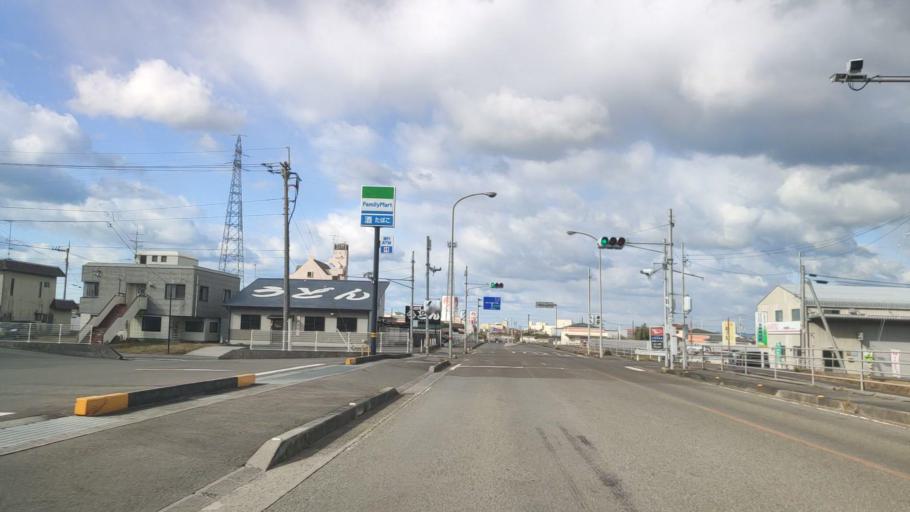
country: JP
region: Ehime
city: Hojo
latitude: 33.9812
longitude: 132.7828
